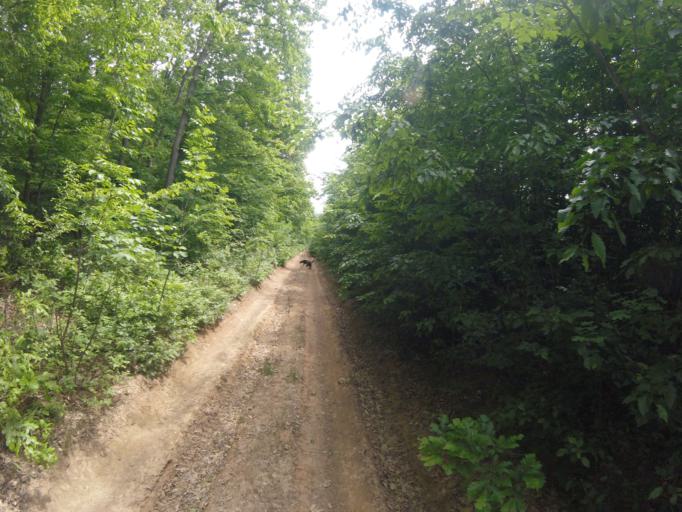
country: HU
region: Pest
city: Telki
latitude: 47.5601
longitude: 18.8457
